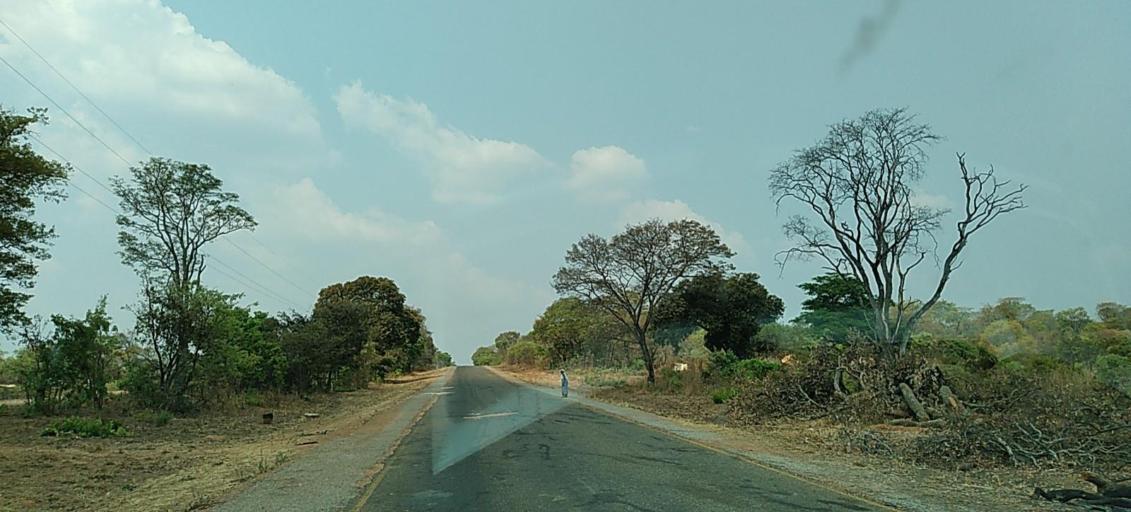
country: ZM
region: North-Western
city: Kabompo
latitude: -13.6193
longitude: 24.1245
